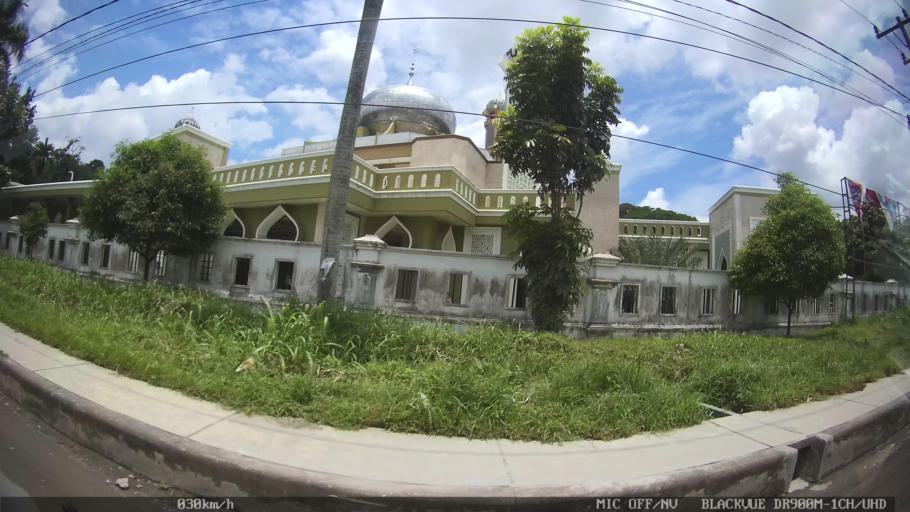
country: ID
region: North Sumatra
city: Medan
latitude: 3.6063
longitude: 98.7192
